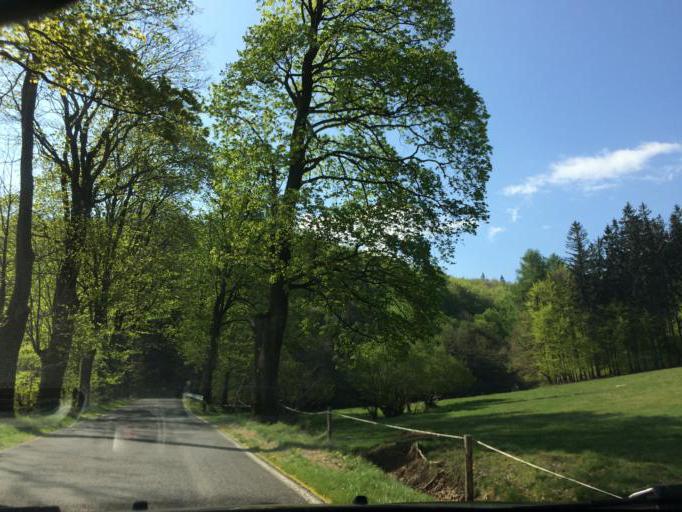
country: PL
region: Lower Silesian Voivodeship
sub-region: Powiat klodzki
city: Jugow
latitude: 50.6661
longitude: 16.5406
